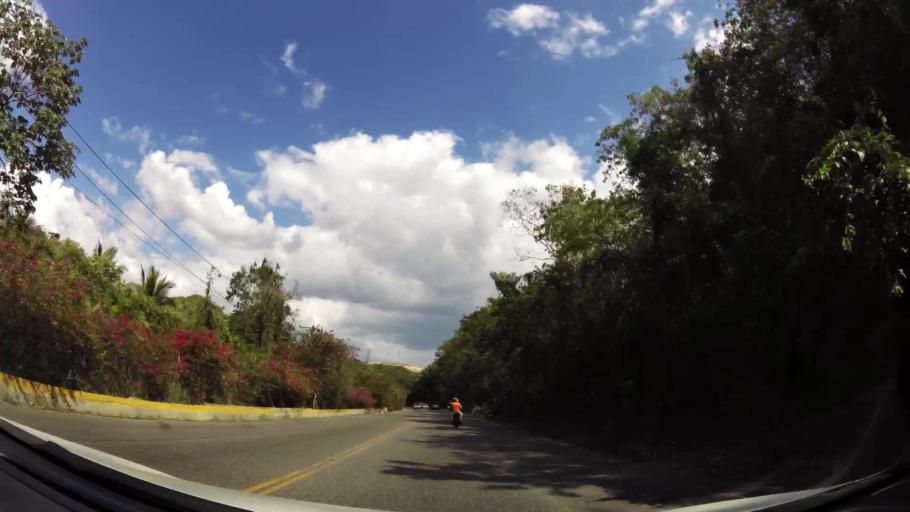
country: DO
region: San Cristobal
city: Bajos de Haina
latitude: 18.4267
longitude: -70.0572
